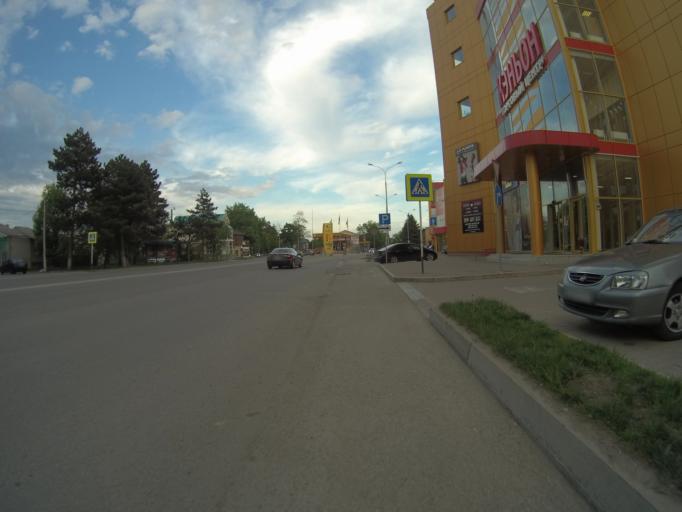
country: RU
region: Stavropol'skiy
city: Yessentuki
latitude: 44.0389
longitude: 42.8693
